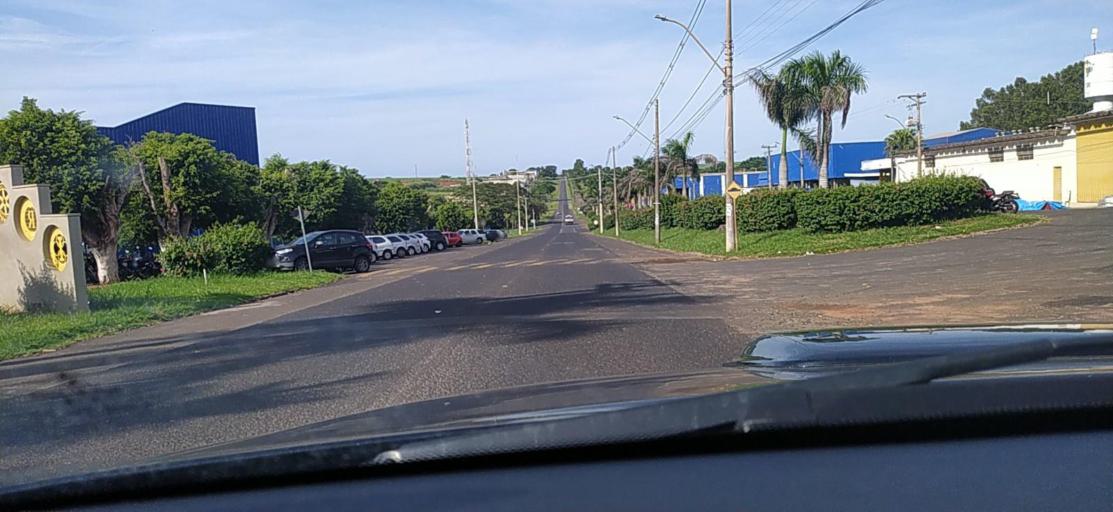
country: BR
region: Sao Paulo
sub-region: Pindorama
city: Pindorama
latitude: -21.1912
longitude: -48.9123
